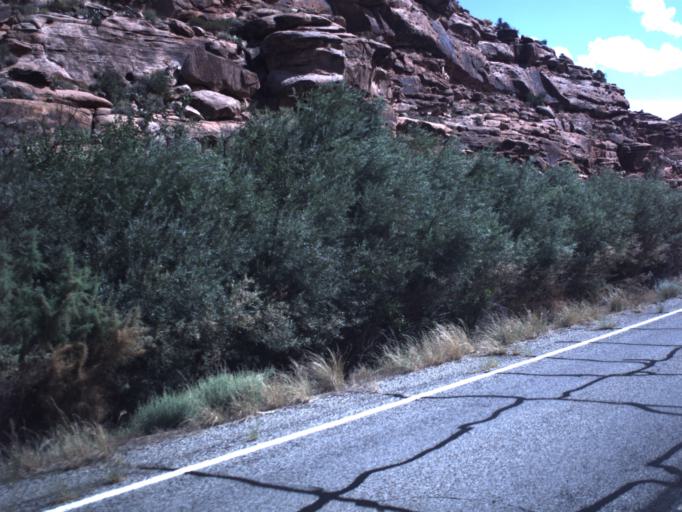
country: US
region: Utah
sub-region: Grand County
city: Moab
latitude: 38.5442
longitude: -109.6321
